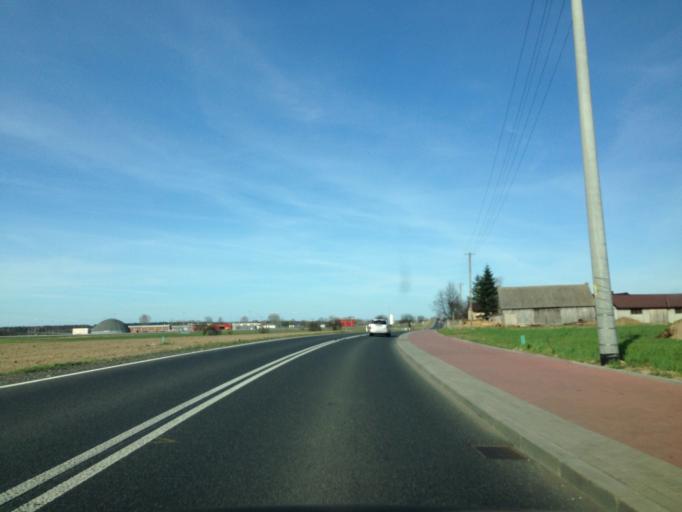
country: PL
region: Lodz Voivodeship
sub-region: Powiat poddebicki
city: Wartkowice
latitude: 51.9897
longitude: 19.0382
